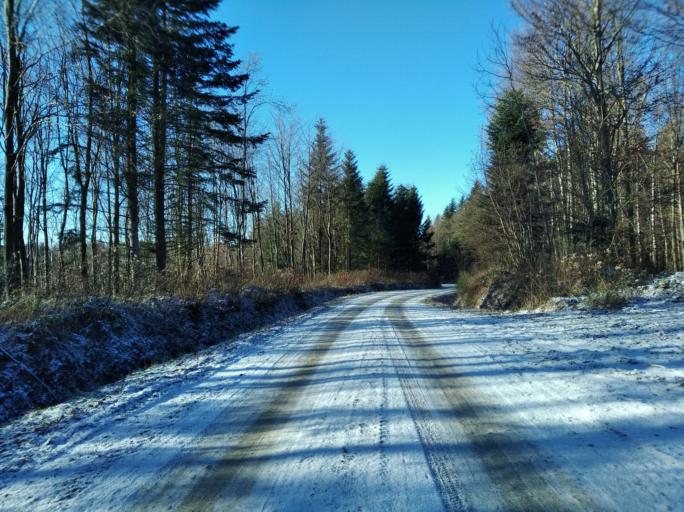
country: PL
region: Subcarpathian Voivodeship
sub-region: Powiat strzyzowski
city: Czudec
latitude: 49.9725
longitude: 21.7960
